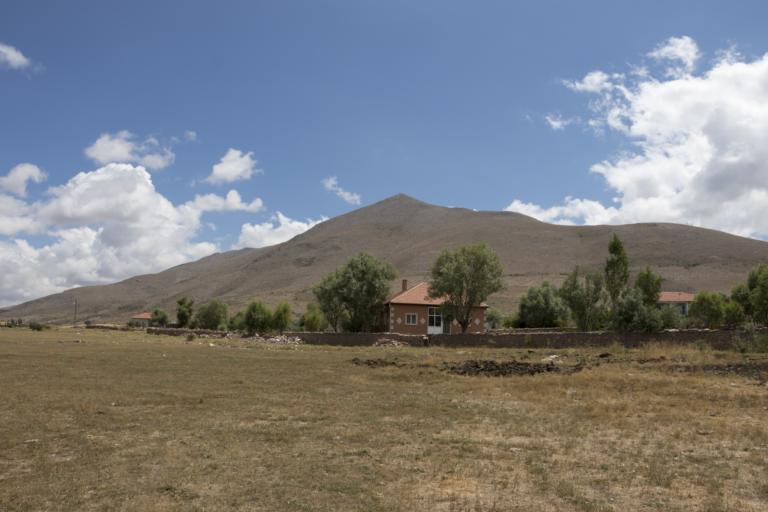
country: TR
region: Kayseri
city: Toklar
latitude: 38.4237
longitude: 36.0968
